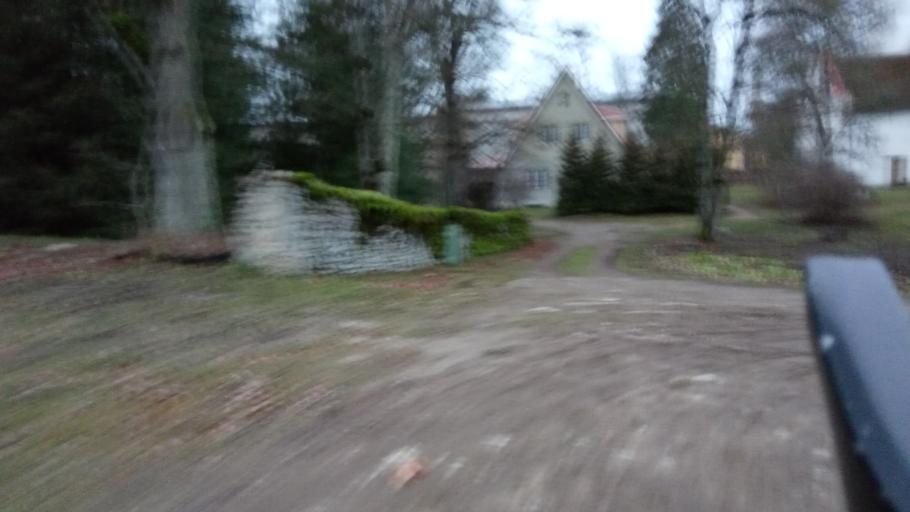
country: EE
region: Harju
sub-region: Kuusalu vald
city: Kuusalu
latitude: 59.4449
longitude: 25.4380
